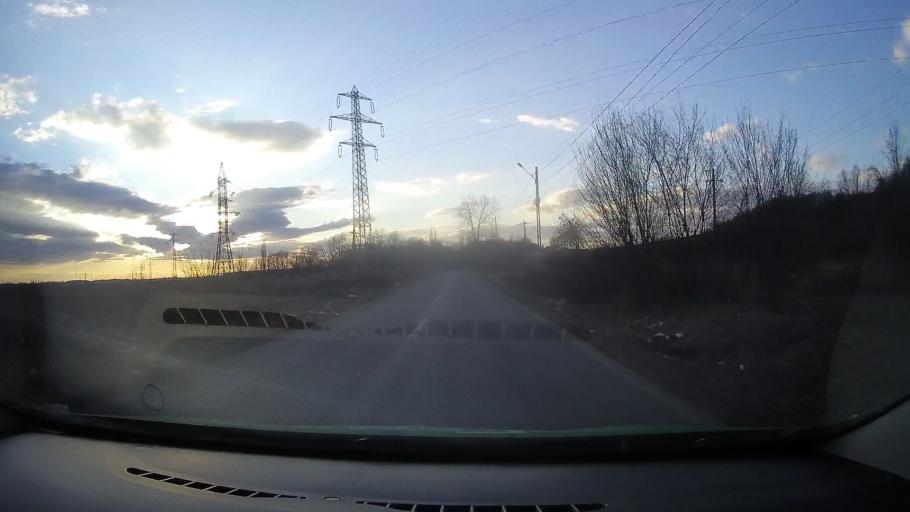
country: RO
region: Dambovita
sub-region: Comuna Gura Ocnitei
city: Gura Ocnitei
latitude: 44.9362
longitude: 25.5878
